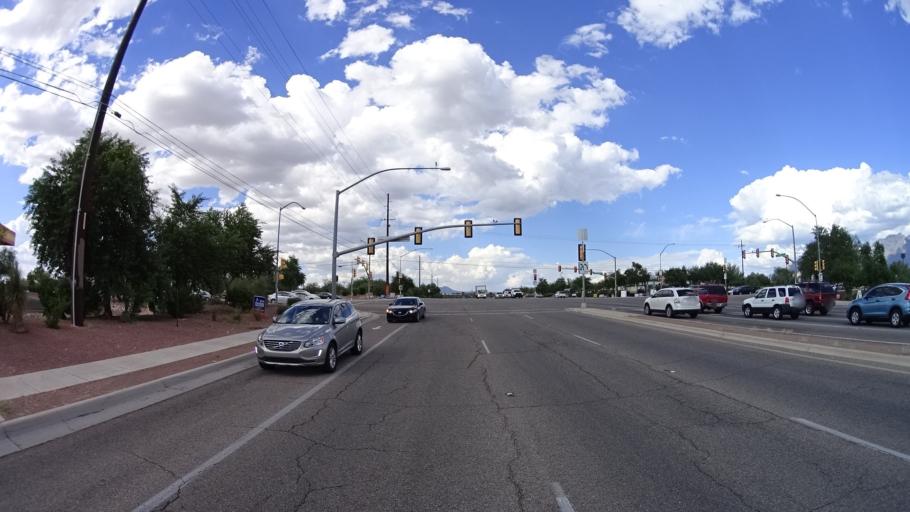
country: US
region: Arizona
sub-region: Pima County
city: Casas Adobes
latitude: 32.3227
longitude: -111.0120
